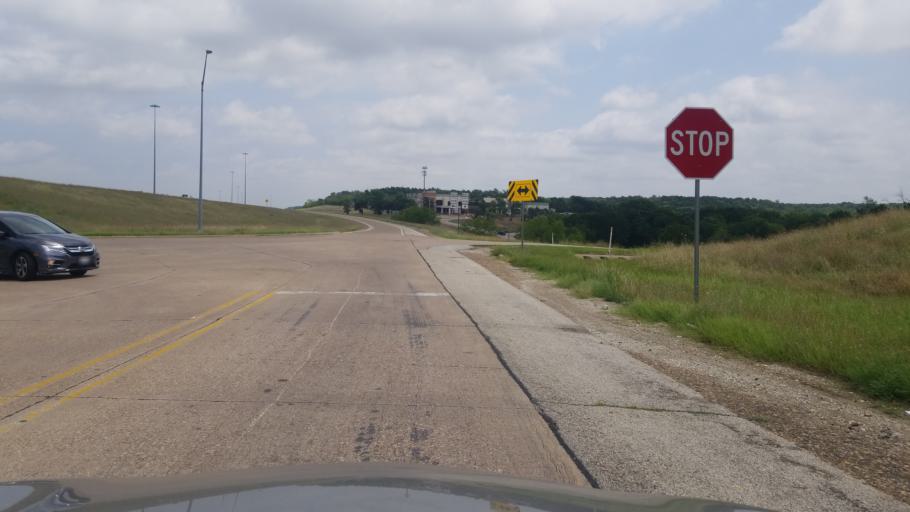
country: US
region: Texas
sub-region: Dallas County
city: Duncanville
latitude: 32.6907
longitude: -96.9378
